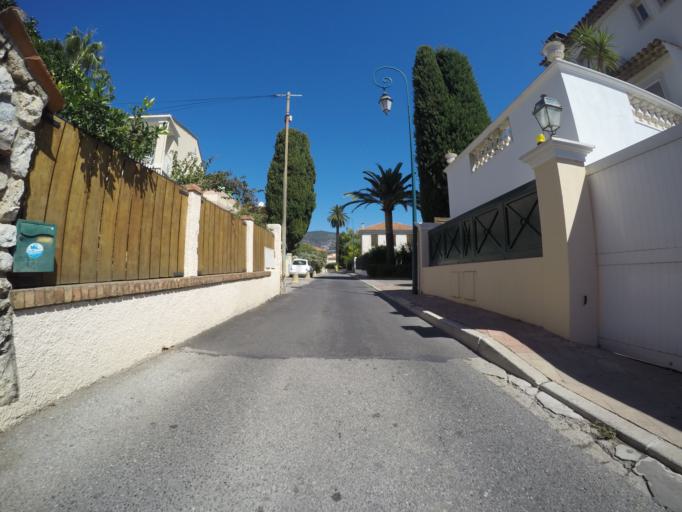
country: FR
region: Provence-Alpes-Cote d'Azur
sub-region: Departement des Alpes-Maritimes
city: Saint-Jean-Cap-Ferrat
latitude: 43.6872
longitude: 7.3336
